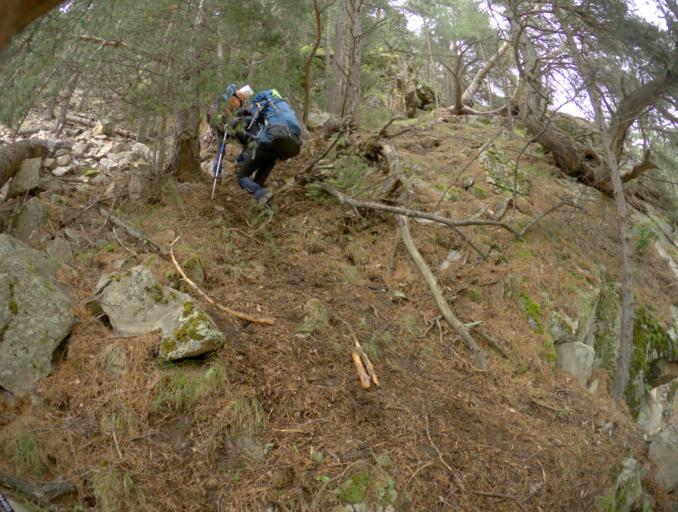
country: RU
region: Karachayevo-Cherkesiya
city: Uchkulan
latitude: 43.4204
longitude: 42.2056
